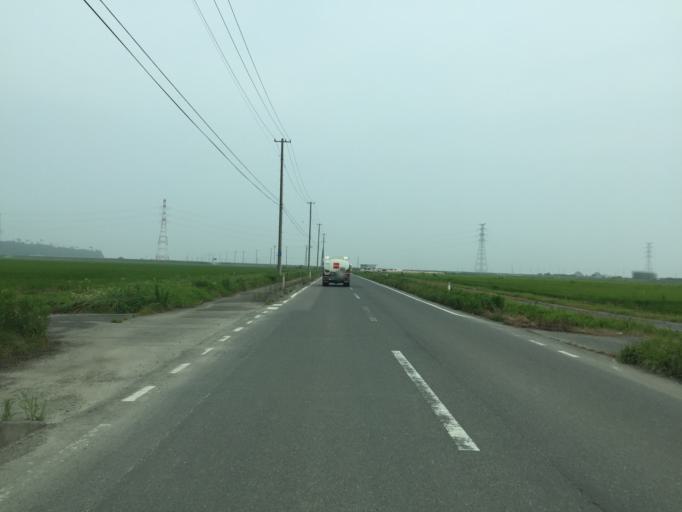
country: JP
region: Fukushima
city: Namie
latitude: 37.6379
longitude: 141.0075
